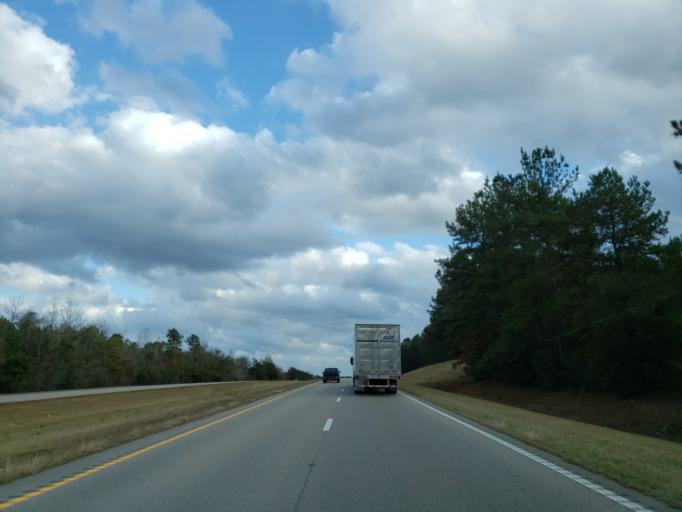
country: US
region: Mississippi
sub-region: Forrest County
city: Petal
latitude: 31.2252
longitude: -89.1835
